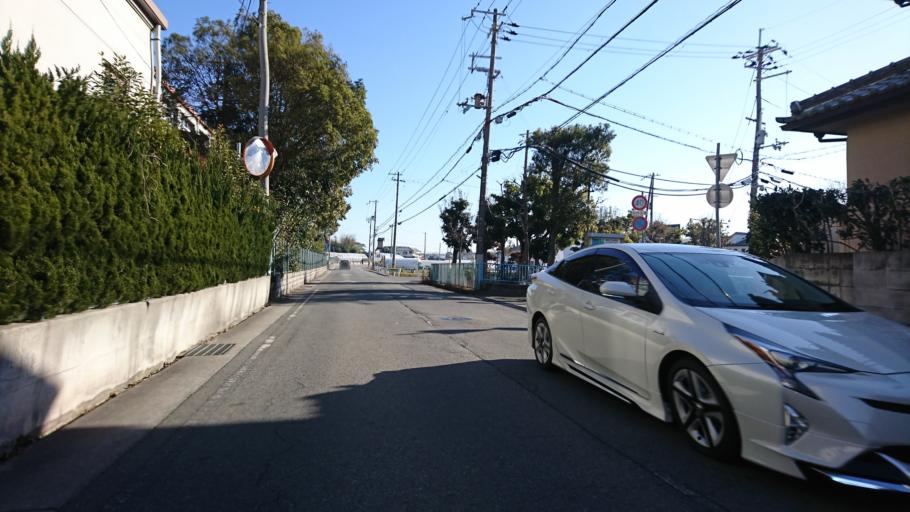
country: JP
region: Hyogo
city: Kakogawacho-honmachi
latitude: 34.7527
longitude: 134.8753
